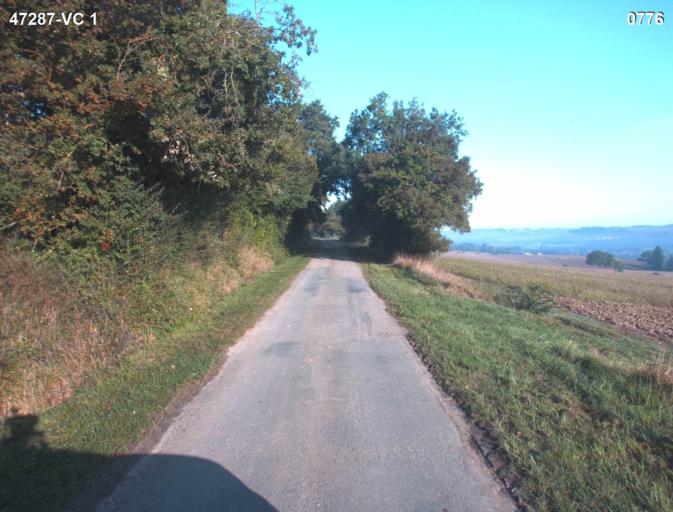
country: FR
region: Aquitaine
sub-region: Departement du Lot-et-Garonne
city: Laplume
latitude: 44.1298
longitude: 0.4545
